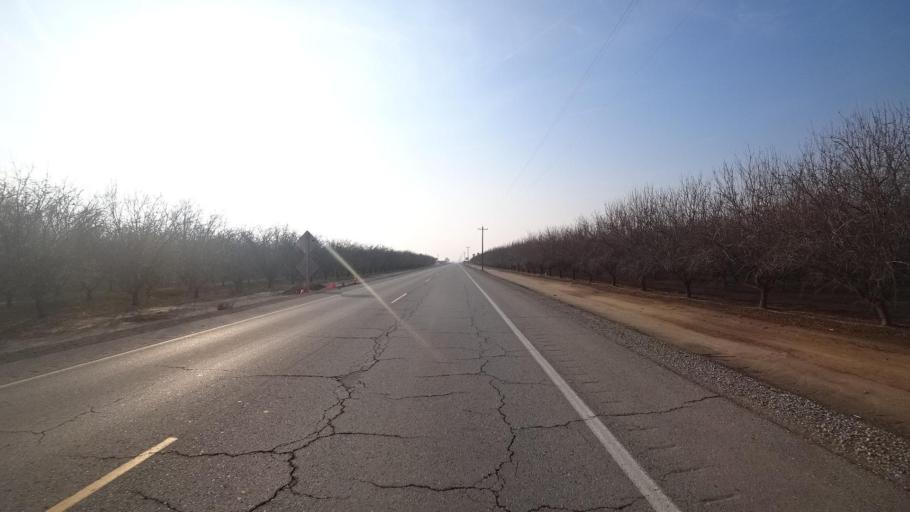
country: US
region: California
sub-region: Kern County
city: Weedpatch
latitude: 35.2043
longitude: -118.9146
